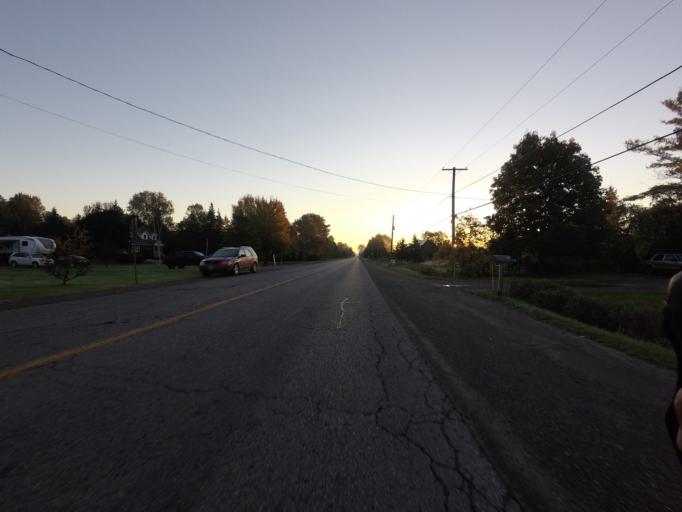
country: CA
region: Ontario
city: Quinte West
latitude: 44.0384
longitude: -77.6494
